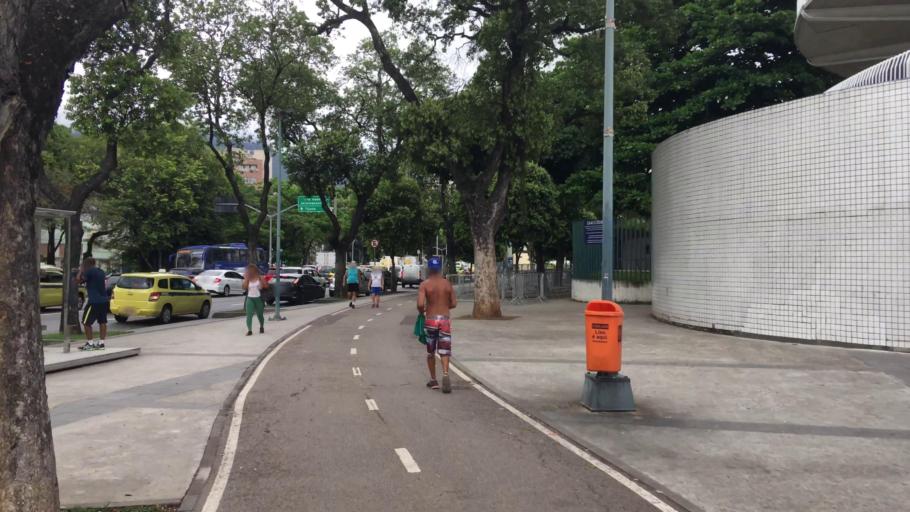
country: BR
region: Rio de Janeiro
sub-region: Rio De Janeiro
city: Rio de Janeiro
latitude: -22.9139
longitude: -43.2283
